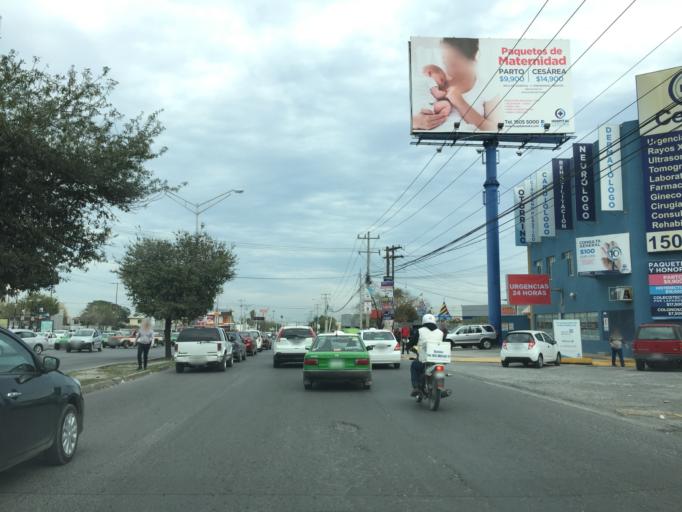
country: MX
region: Nuevo Leon
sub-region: Juarez
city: Jardines de la Silla (Jardines)
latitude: 25.6562
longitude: -100.1826
